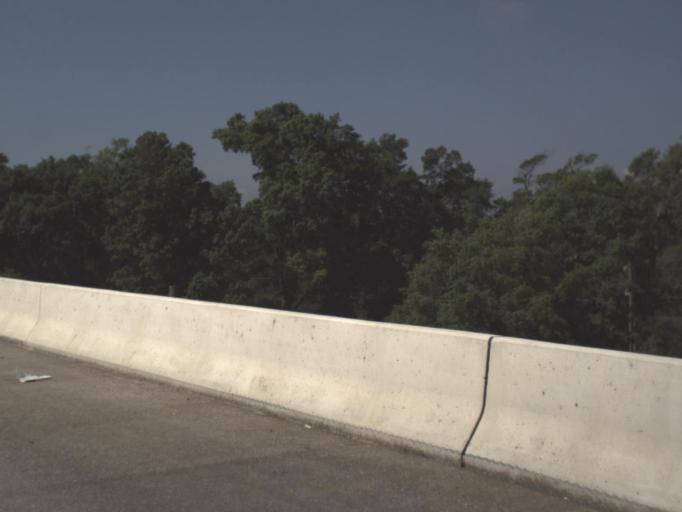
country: US
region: Florida
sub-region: Escambia County
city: Pensacola
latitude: 30.4325
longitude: -87.2160
